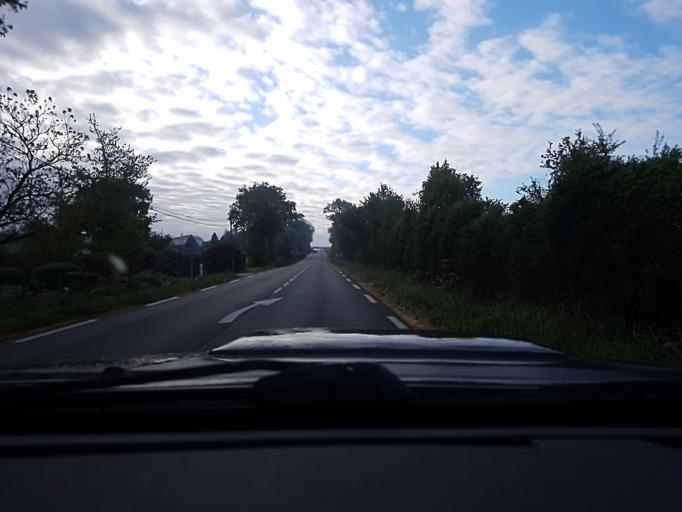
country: FR
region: Pays de la Loire
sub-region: Departement de la Vendee
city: Mache
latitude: 46.7605
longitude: -1.6478
